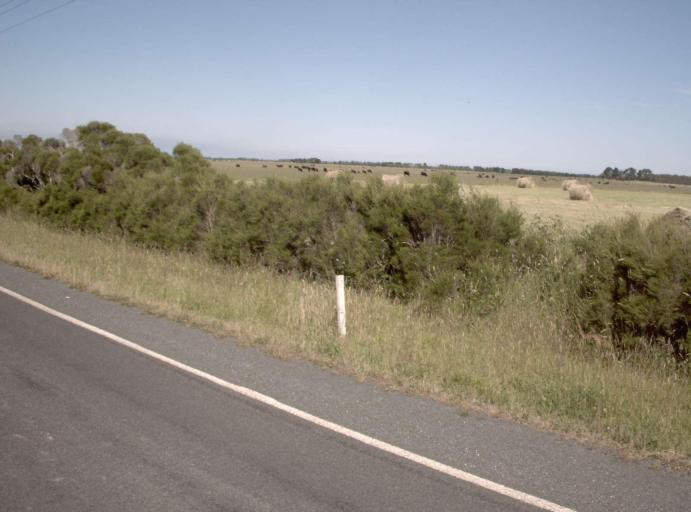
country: AU
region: Victoria
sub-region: Latrobe
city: Traralgon
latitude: -38.6321
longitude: 146.5904
